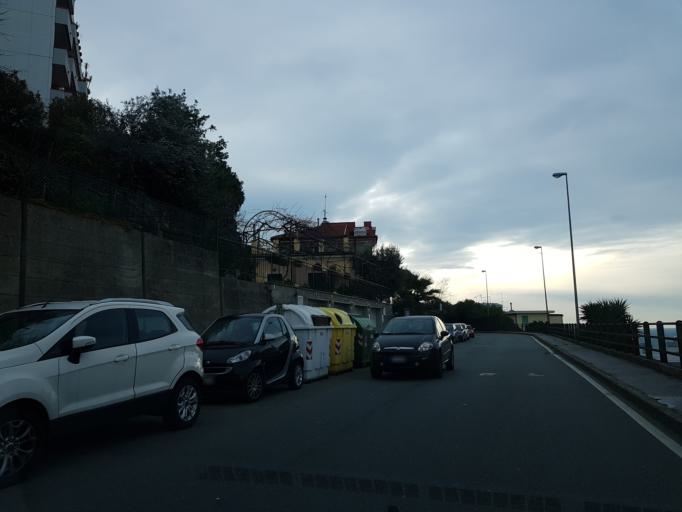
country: IT
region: Liguria
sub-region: Provincia di Genova
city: Mele
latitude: 44.4269
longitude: 8.7996
